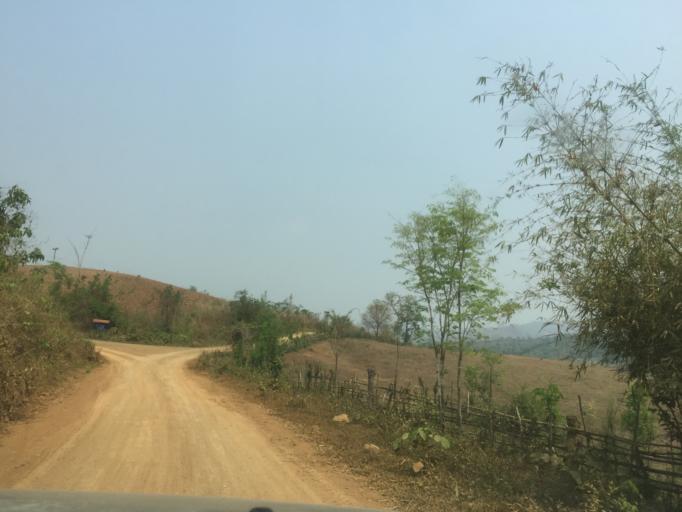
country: LA
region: Xiagnabouli
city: Muang Kenthao
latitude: 17.7893
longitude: 101.2550
